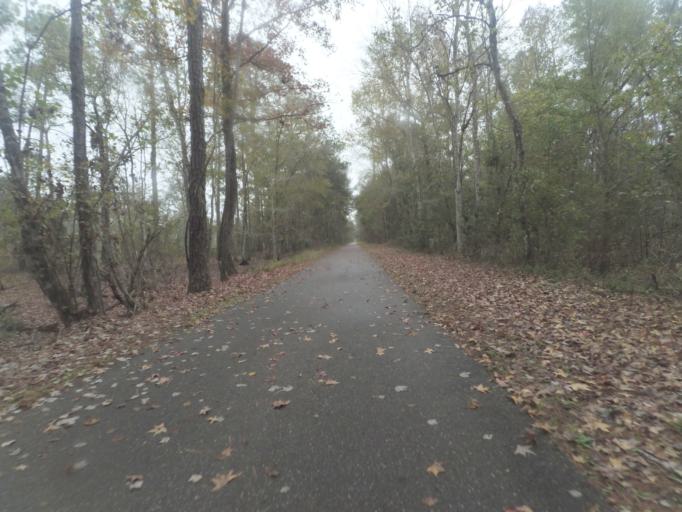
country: US
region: Florida
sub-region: Alachua County
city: Hawthorne
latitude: 29.5983
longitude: -82.1487
